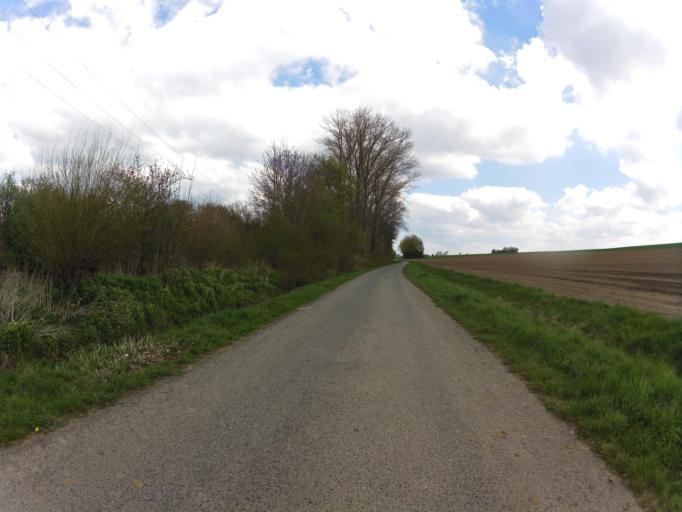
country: DE
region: Bavaria
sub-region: Regierungsbezirk Unterfranken
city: Giebelstadt
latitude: 49.6502
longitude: 9.9248
